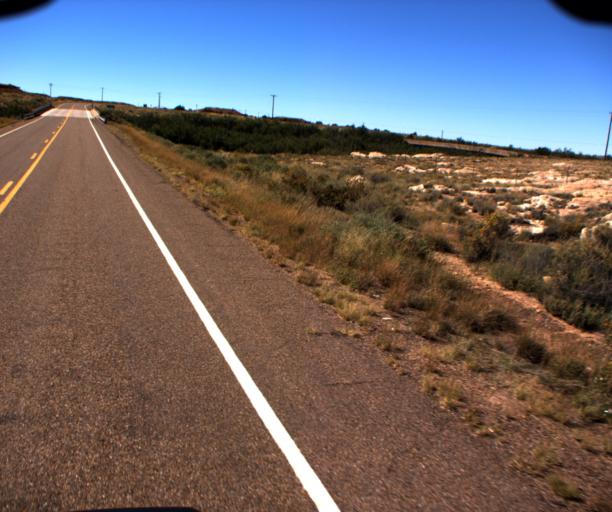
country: US
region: Arizona
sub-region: Navajo County
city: Holbrook
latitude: 34.8831
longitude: -110.1073
